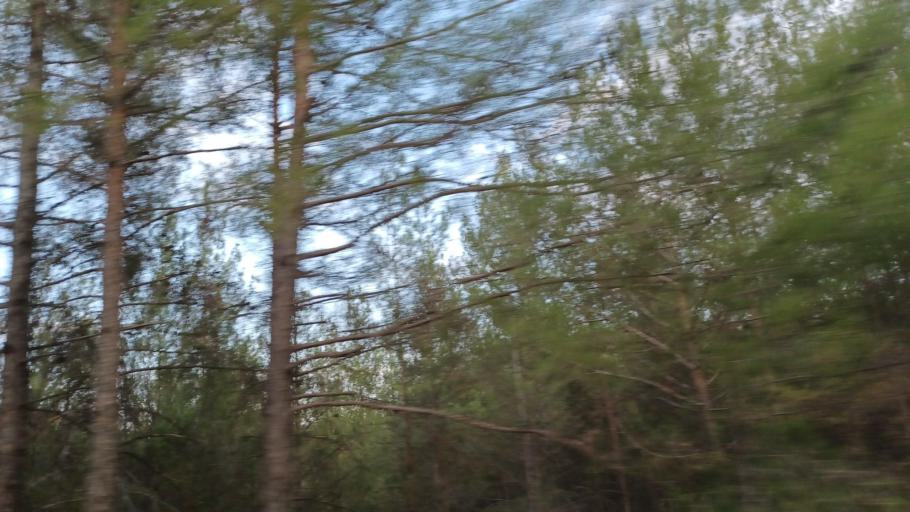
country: CY
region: Limassol
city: Kyperounta
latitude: 34.9372
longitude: 32.9324
